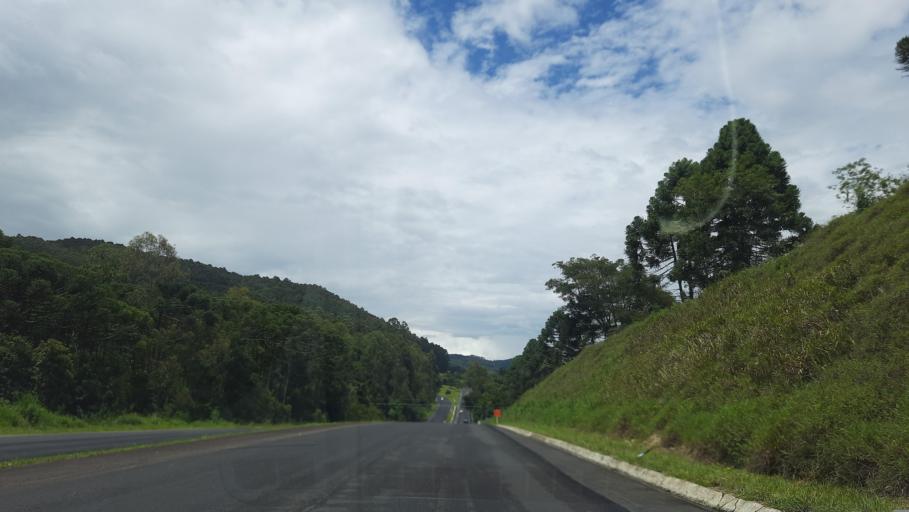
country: BR
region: Minas Gerais
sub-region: Pocos De Caldas
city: Pocos de Caldas
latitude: -21.8056
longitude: -46.6529
